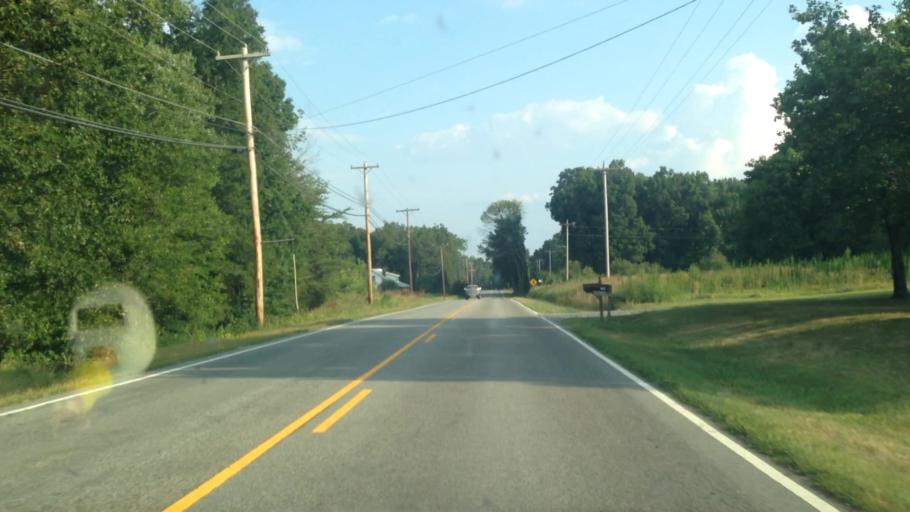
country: US
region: North Carolina
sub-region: Guilford County
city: High Point
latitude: 35.9982
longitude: -80.0630
